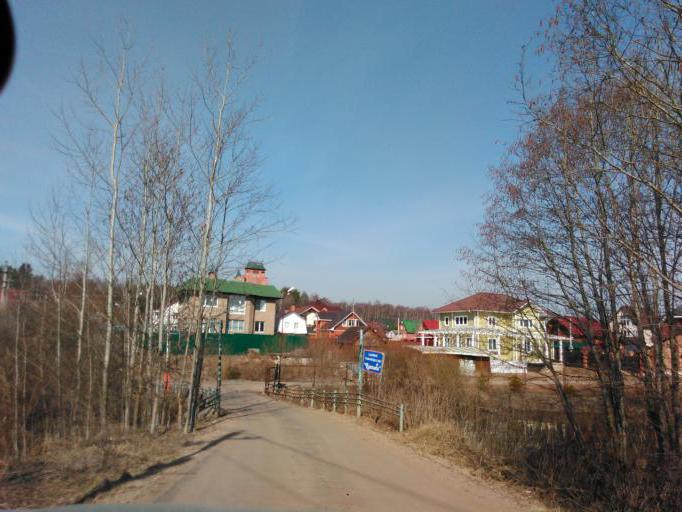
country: RU
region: Moskovskaya
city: Opalikha
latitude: 55.8735
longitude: 37.2516
